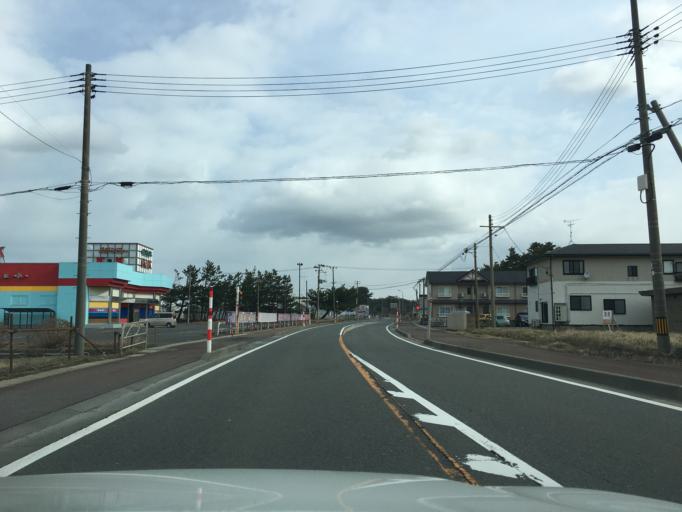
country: JP
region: Yamagata
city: Yuza
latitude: 39.2211
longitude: 139.9017
